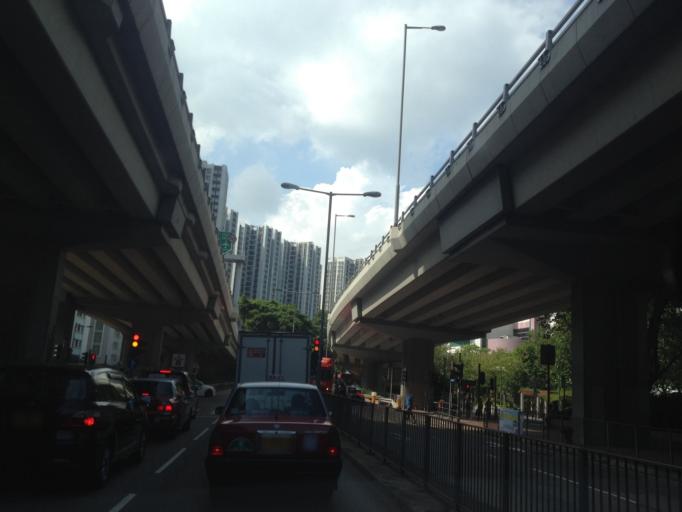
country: HK
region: Wanchai
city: Wan Chai
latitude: 22.2833
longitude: 114.2229
